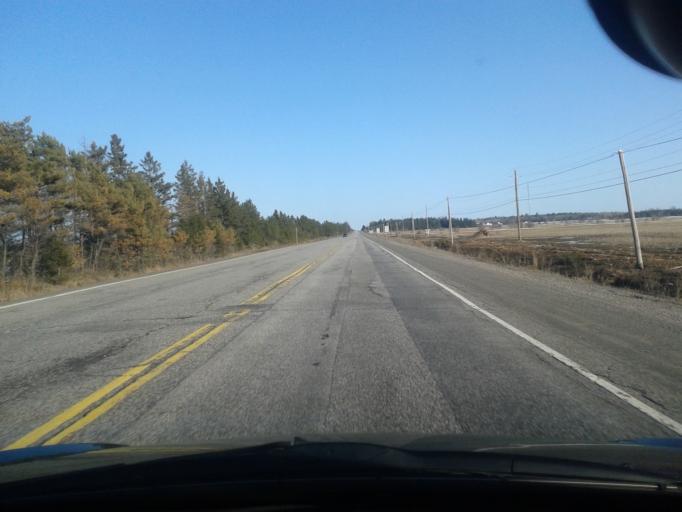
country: CA
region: Ontario
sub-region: Nipissing District
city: North Bay
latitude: 46.4041
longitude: -80.0317
